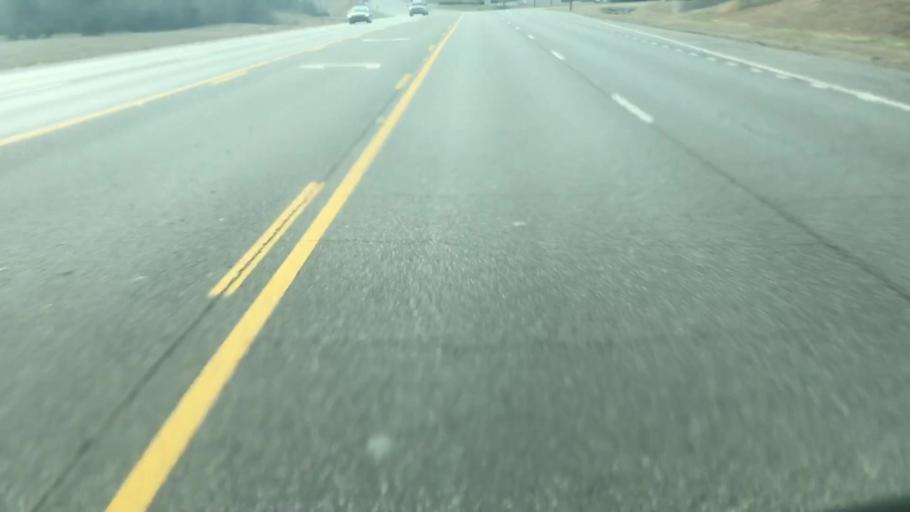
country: US
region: Alabama
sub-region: Walker County
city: Jasper
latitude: 33.8213
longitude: -87.2339
